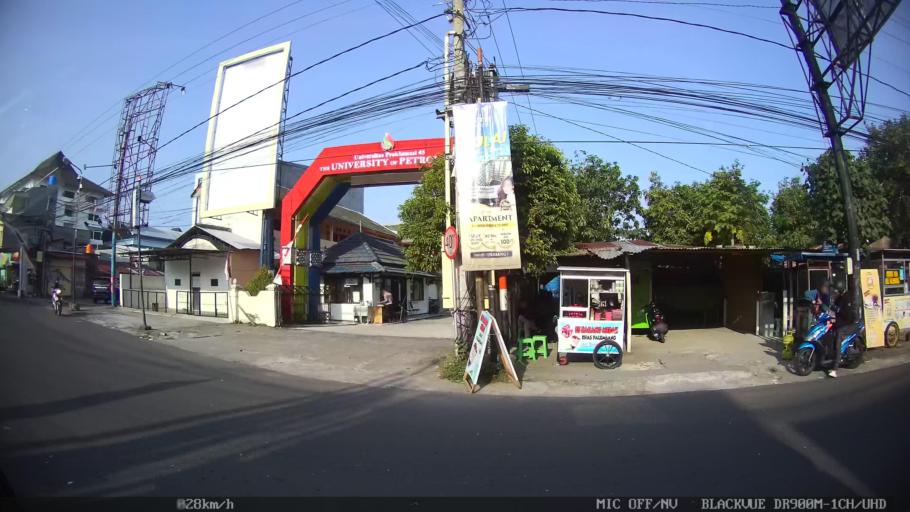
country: ID
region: Daerah Istimewa Yogyakarta
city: Depok
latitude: -7.7741
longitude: 110.4159
